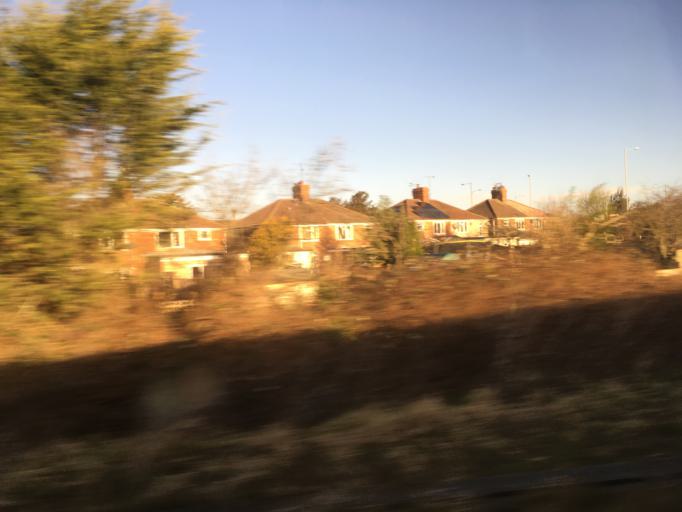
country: GB
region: England
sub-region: Borough of Swindon
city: Swindon
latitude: 51.5736
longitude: -1.7547
